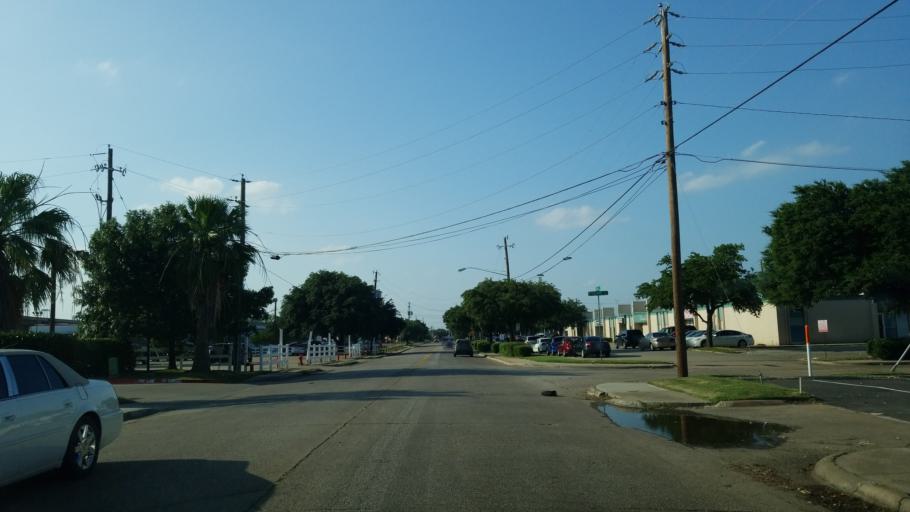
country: US
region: Texas
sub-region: Dallas County
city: Farmers Branch
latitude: 32.8773
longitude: -96.8960
